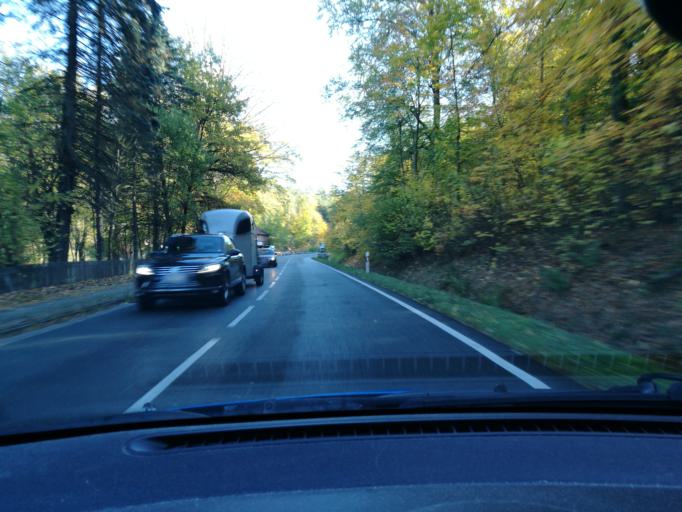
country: DE
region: Lower Saxony
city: Gohrde
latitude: 53.1383
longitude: 10.8804
